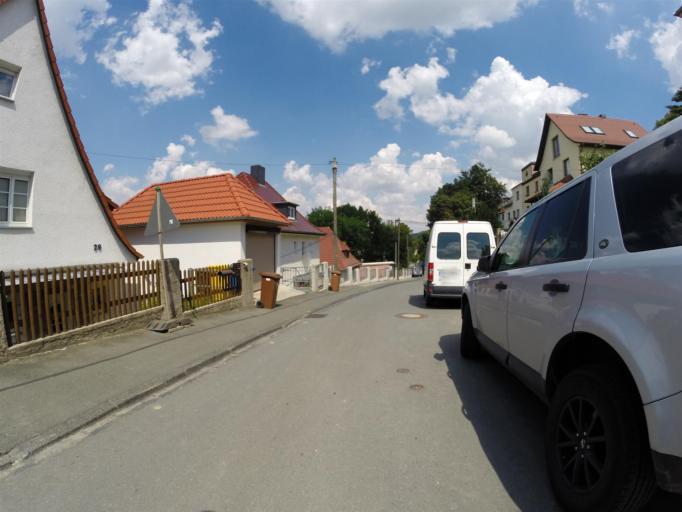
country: DE
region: Thuringia
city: Jena
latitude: 50.9267
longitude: 11.5985
